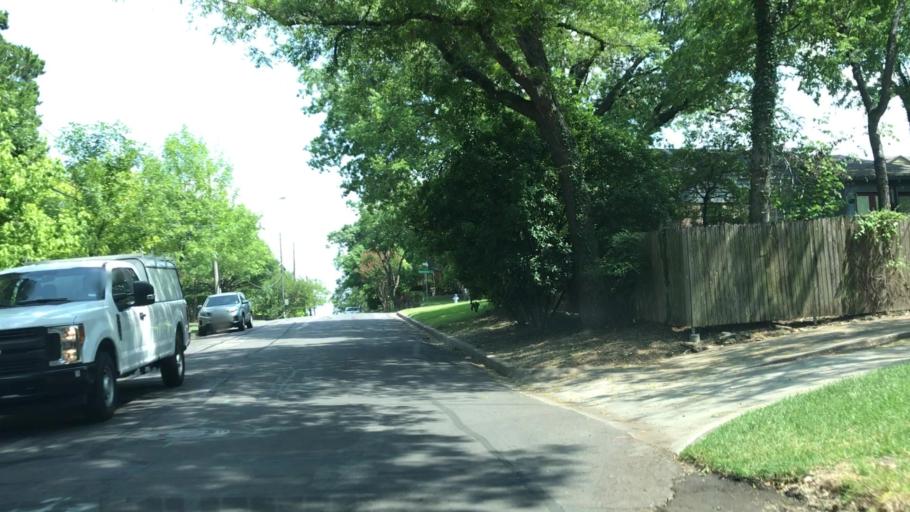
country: US
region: Texas
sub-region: Dallas County
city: Highland Park
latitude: 32.8066
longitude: -96.7376
